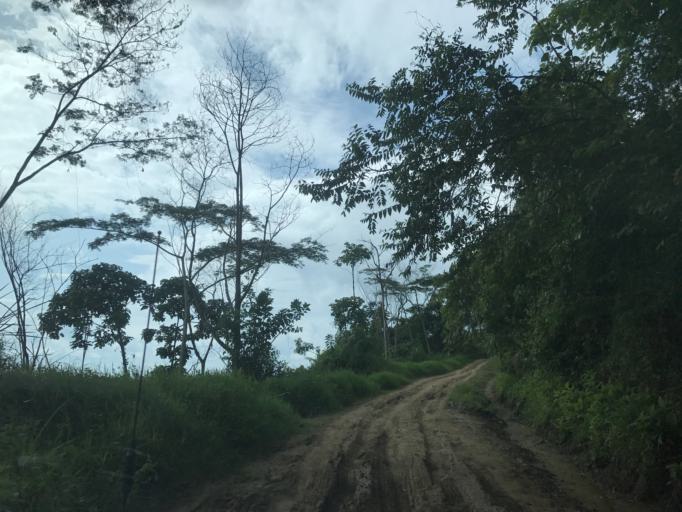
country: CO
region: Valle del Cauca
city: Obando
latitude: 4.5748
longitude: -75.8868
